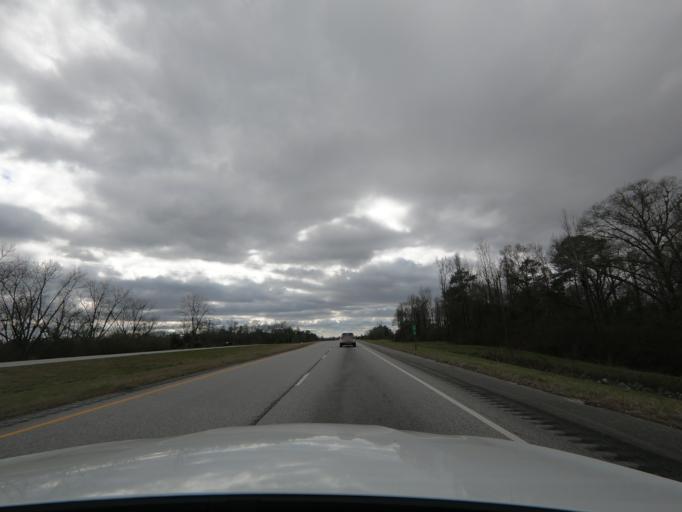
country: US
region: Alabama
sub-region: Russell County
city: Ladonia
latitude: 32.2583
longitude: -85.1630
